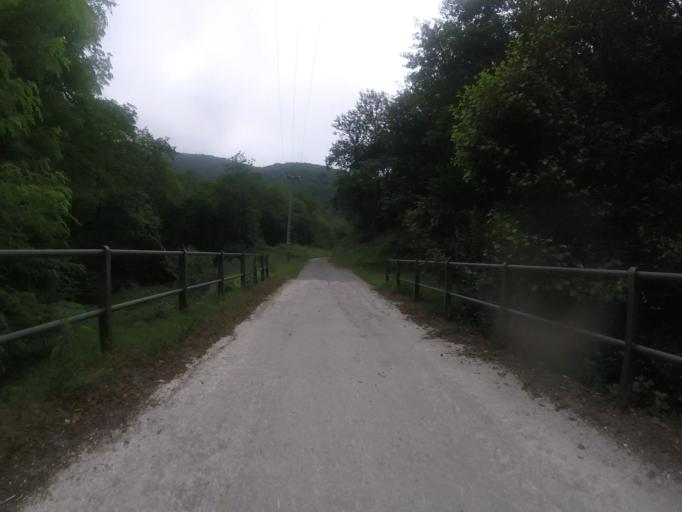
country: ES
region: Navarre
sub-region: Provincia de Navarra
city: Areso
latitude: 43.1169
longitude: -1.9367
